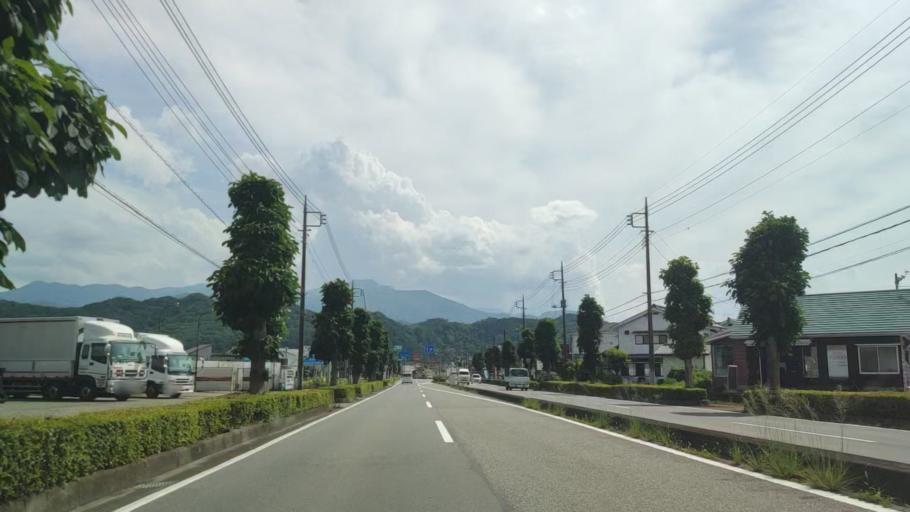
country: JP
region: Gunma
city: Tomioka
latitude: 36.2493
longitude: 138.8602
